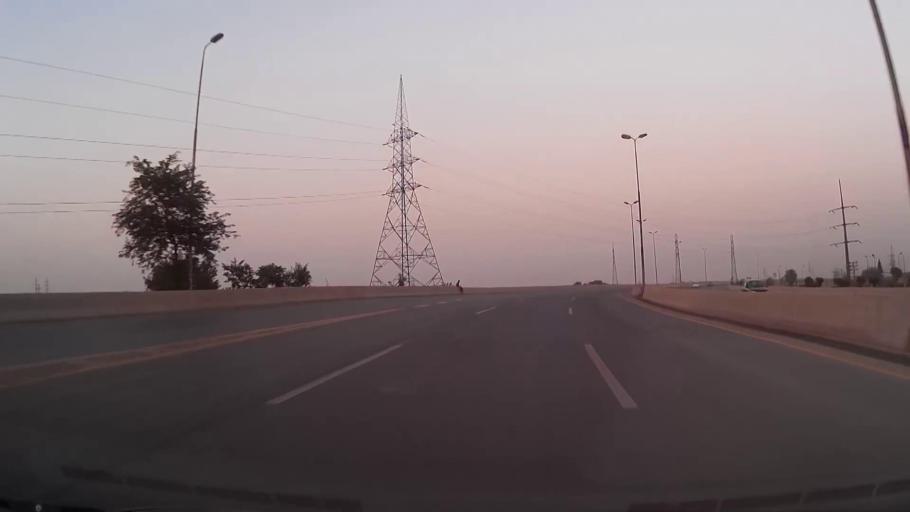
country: PK
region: Punjab
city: Lahore
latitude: 31.6099
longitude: 74.3084
